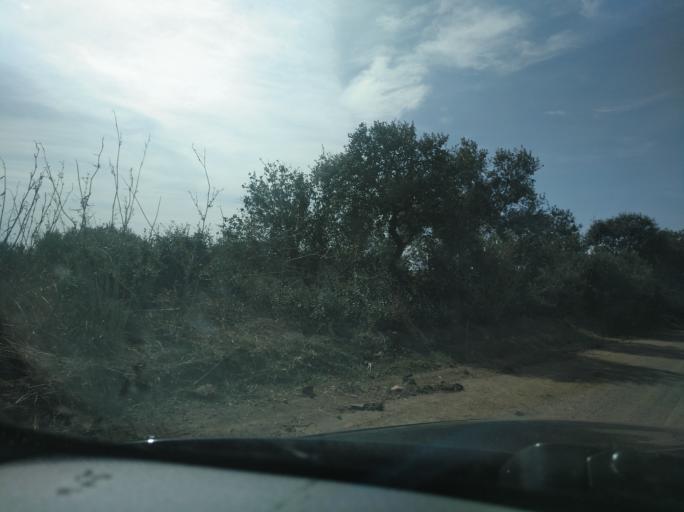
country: PT
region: Portalegre
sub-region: Campo Maior
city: Campo Maior
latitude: 39.0488
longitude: -7.0534
